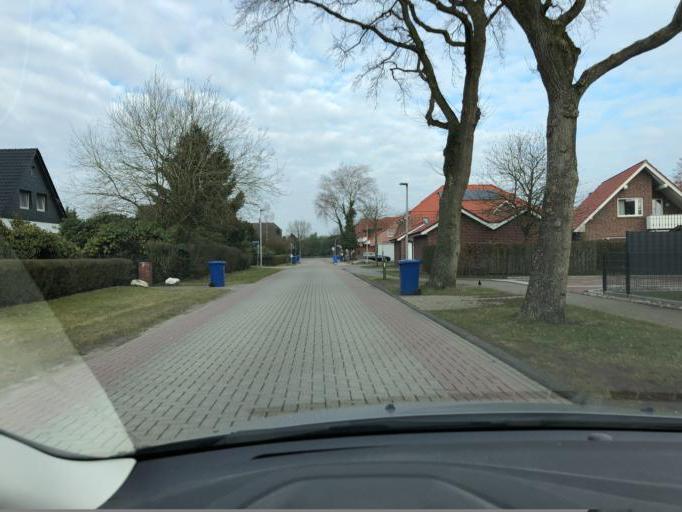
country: DE
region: Lower Saxony
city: Bad Zwischenahn
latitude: 53.1796
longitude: 8.0452
